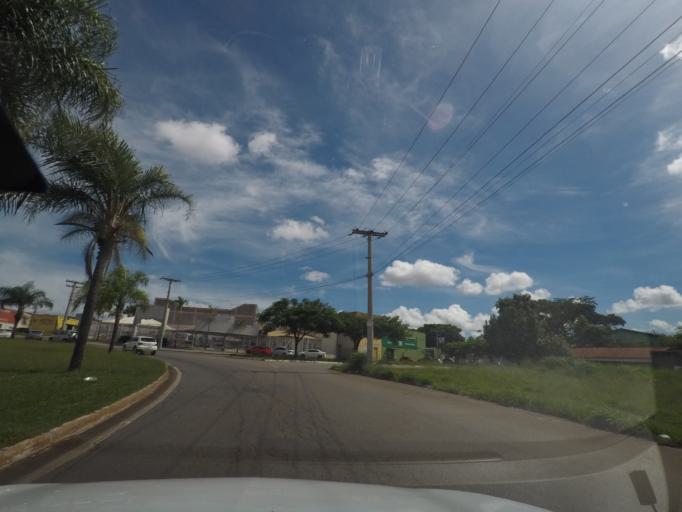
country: BR
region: Goias
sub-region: Goiania
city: Goiania
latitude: -16.7438
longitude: -49.3302
